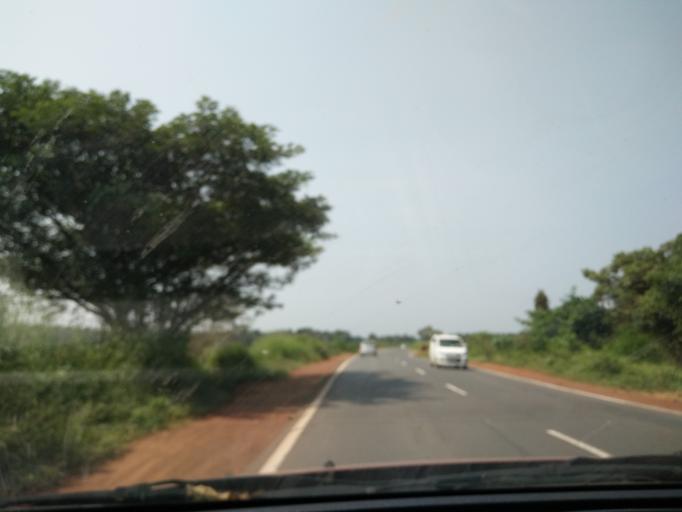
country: IN
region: Goa
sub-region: South Goa
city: Raia
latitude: 15.3036
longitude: 73.9599
